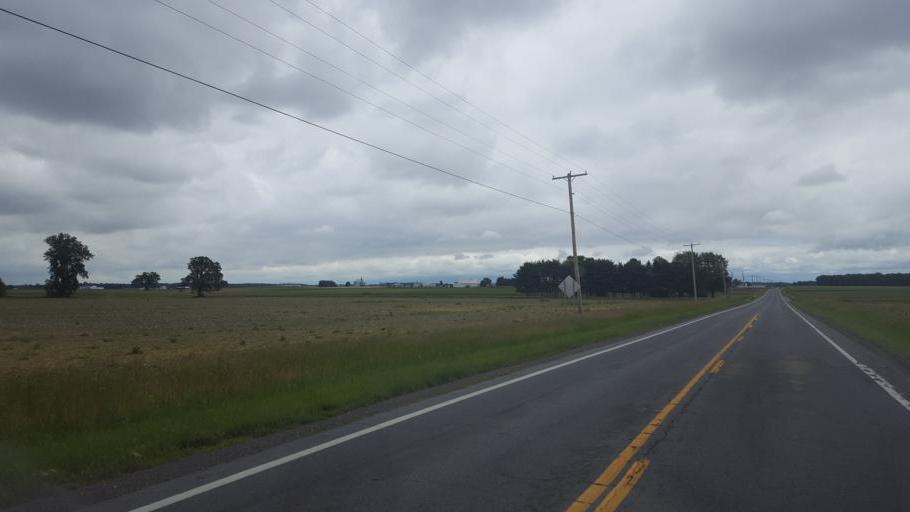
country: US
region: Ohio
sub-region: Crawford County
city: Bucyrus
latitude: 40.7794
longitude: -82.9295
